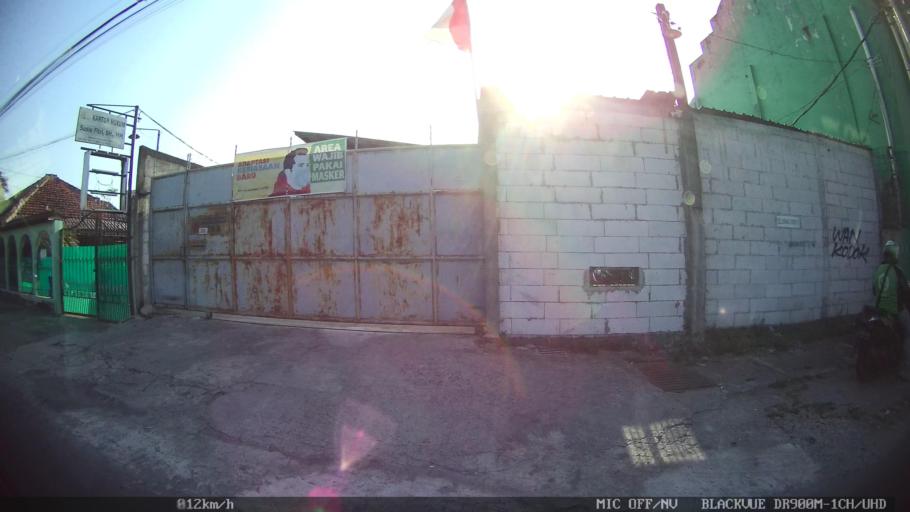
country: ID
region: Daerah Istimewa Yogyakarta
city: Gamping Lor
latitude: -7.7993
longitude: 110.3320
